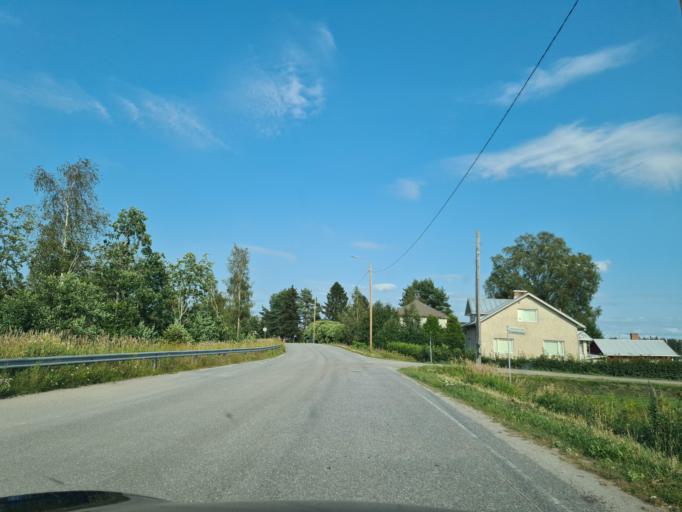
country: FI
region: Ostrobothnia
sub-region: Vaasa
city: Ristinummi
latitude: 63.0319
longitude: 21.8577
